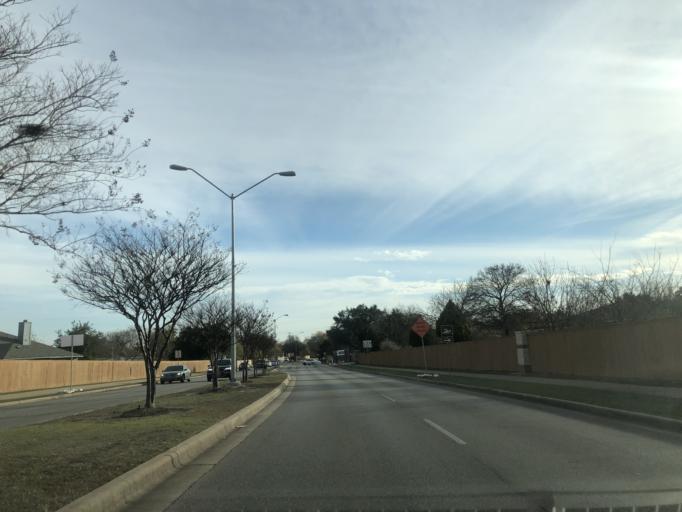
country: US
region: Texas
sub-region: Travis County
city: Windemere
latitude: 30.4618
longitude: -97.6345
